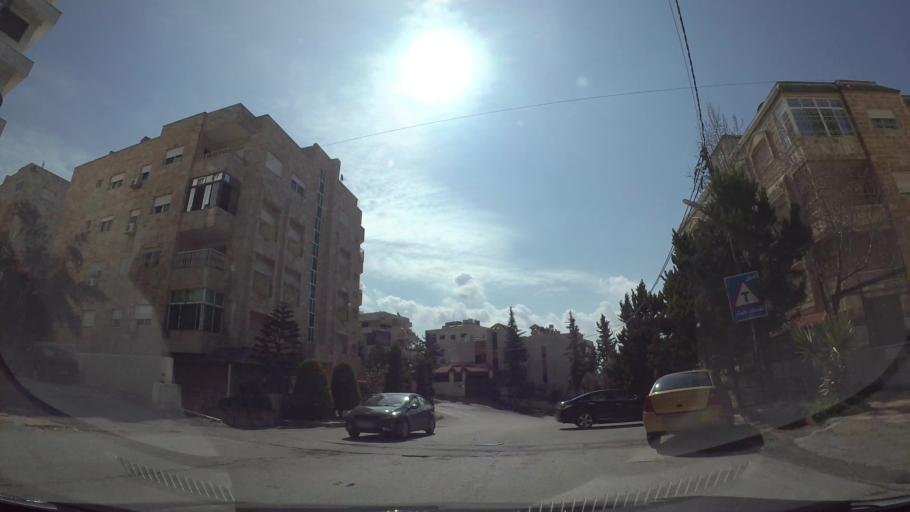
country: JO
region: Amman
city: Al Jubayhah
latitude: 31.9925
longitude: 35.8942
